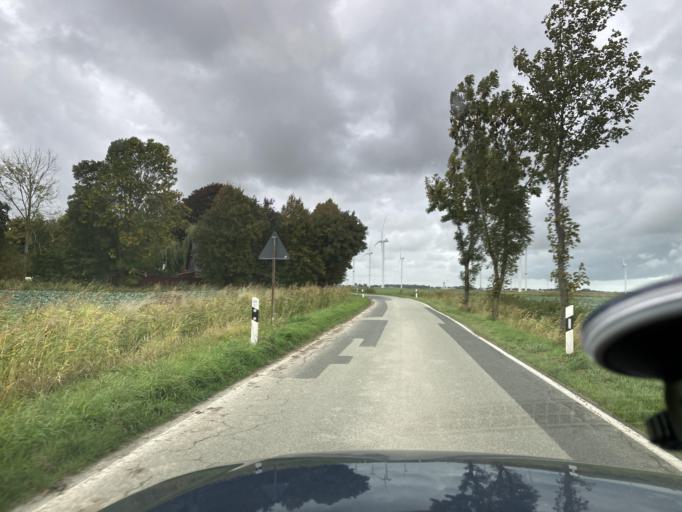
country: DE
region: Schleswig-Holstein
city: Norderwohrden
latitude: 54.1933
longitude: 9.0011
